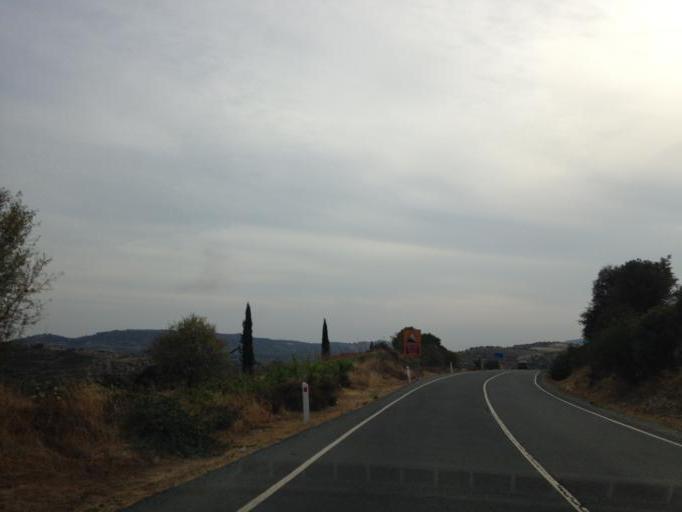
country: CY
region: Limassol
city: Pachna
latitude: 34.8186
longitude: 32.7975
